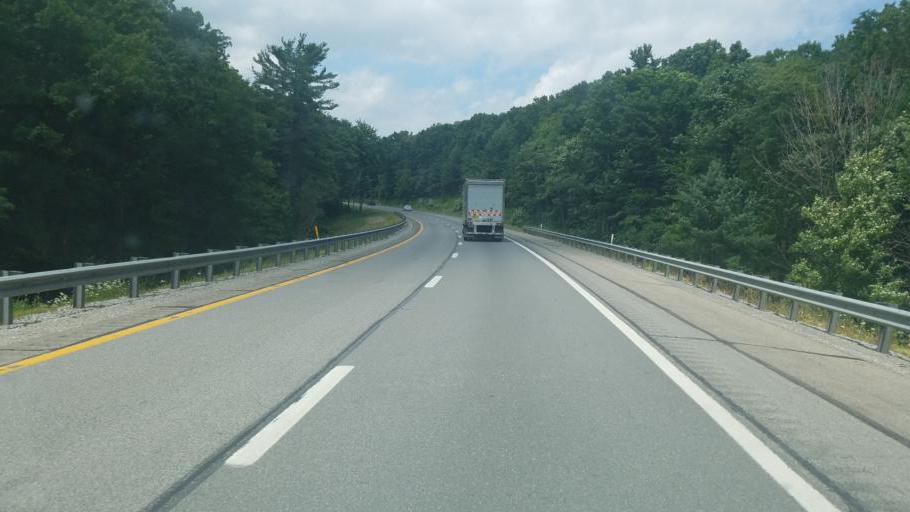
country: US
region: West Virginia
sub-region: Raleigh County
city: Shady Spring
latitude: 37.6725
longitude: -81.1137
